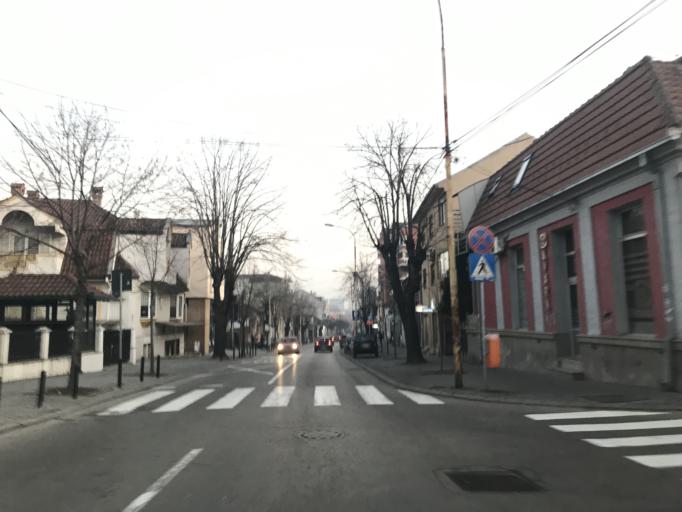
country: RS
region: Central Serbia
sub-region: Sumadijski Okrug
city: Kragujevac
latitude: 44.0149
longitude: 20.9123
